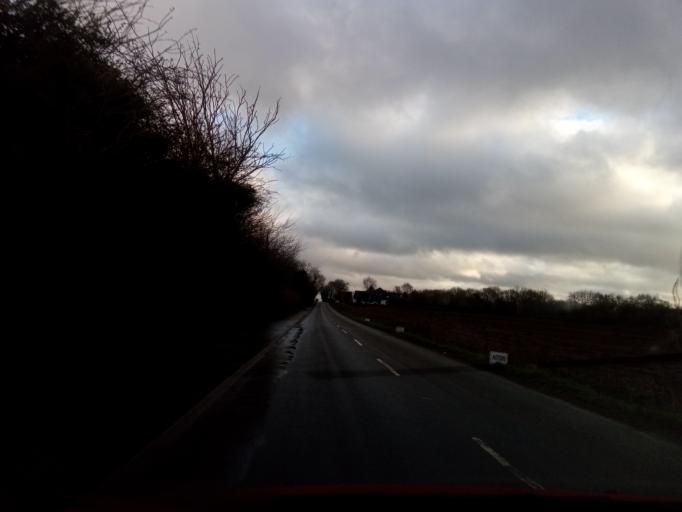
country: GB
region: England
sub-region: Derbyshire
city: Melbourne
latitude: 52.8493
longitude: -1.4152
